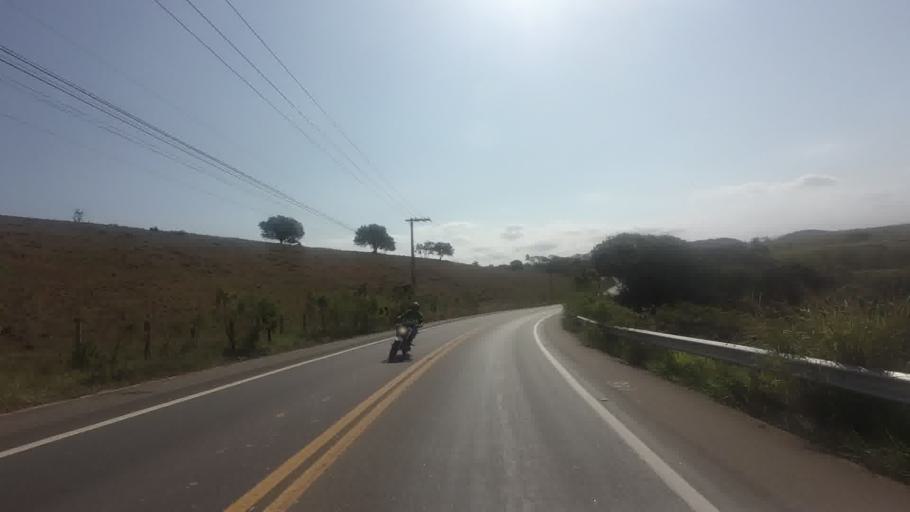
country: BR
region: Espirito Santo
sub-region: Piuma
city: Piuma
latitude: -20.8062
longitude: -40.6698
